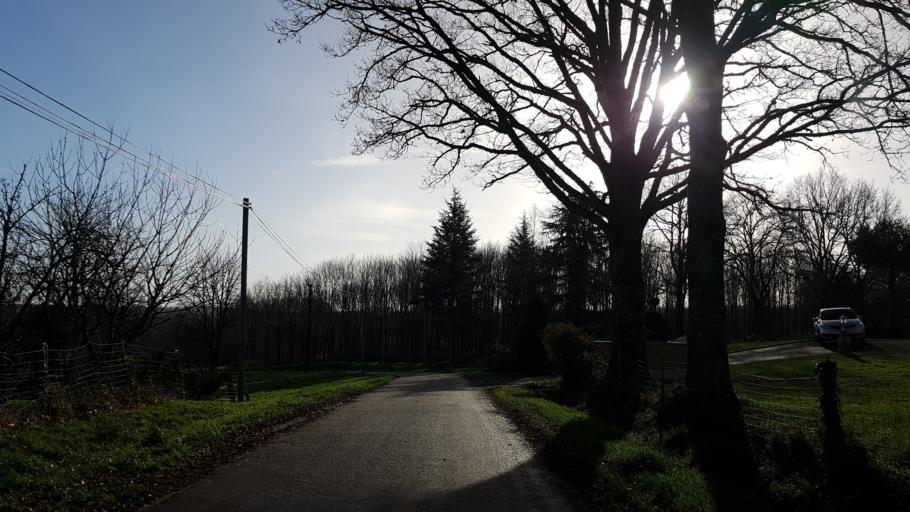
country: FR
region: Poitou-Charentes
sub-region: Departement de la Charente
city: Etagnac
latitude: 45.9327
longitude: 0.7903
